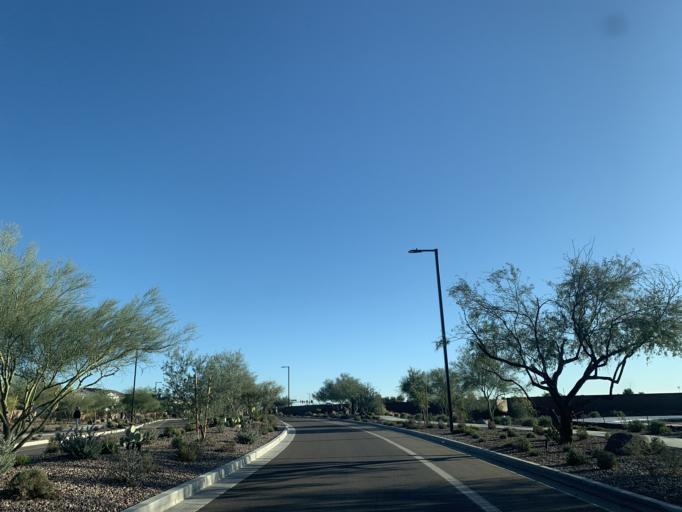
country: US
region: Arizona
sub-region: Maricopa County
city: Cave Creek
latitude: 33.6866
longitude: -112.0148
